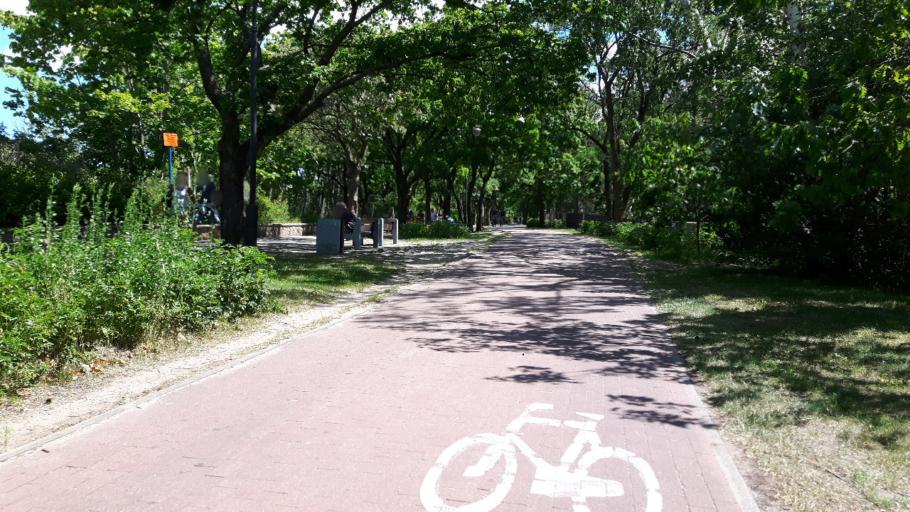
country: PL
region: Pomeranian Voivodeship
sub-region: Sopot
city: Sopot
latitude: 54.4284
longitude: 18.5930
